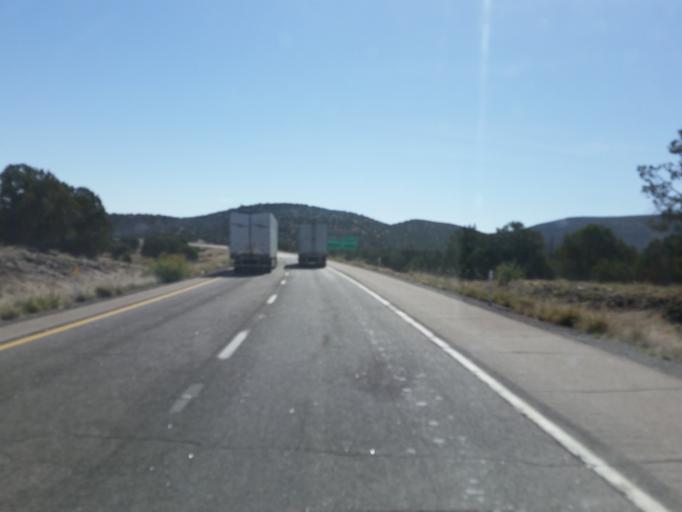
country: US
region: Arizona
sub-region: Mohave County
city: Peach Springs
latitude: 35.1811
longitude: -113.4576
